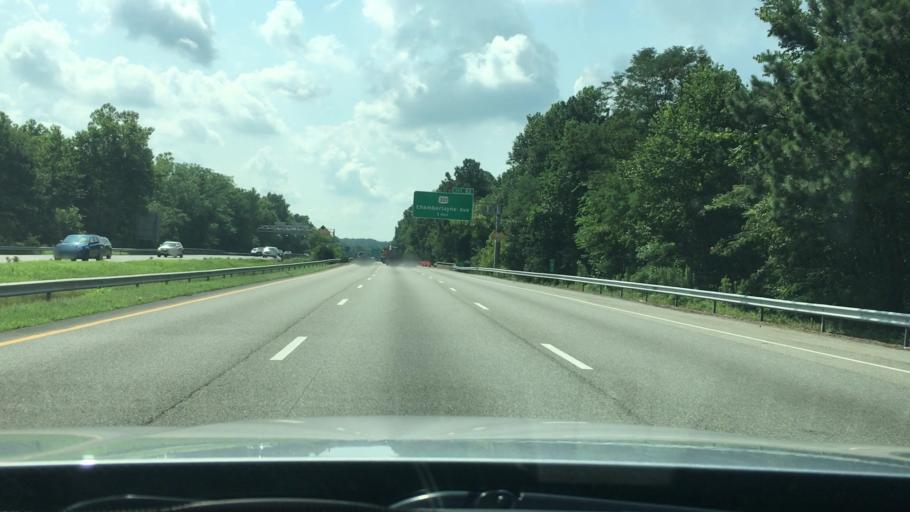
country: US
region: Virginia
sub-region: Henrico County
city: Chamberlayne
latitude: 37.6307
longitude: -77.4498
